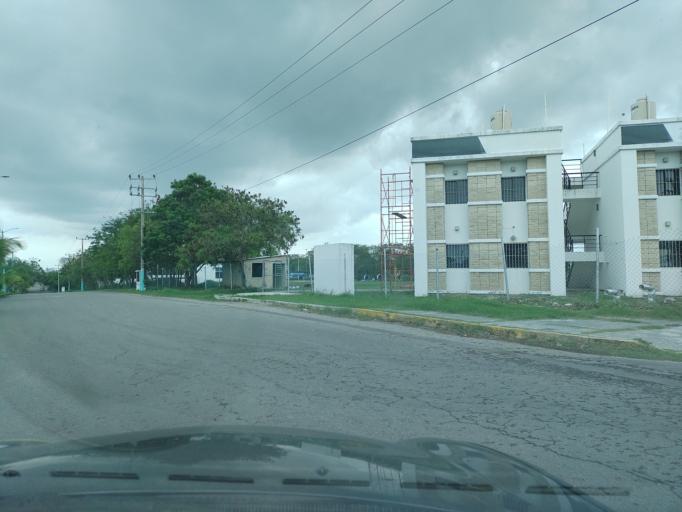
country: MX
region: Quintana Roo
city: Chetumal
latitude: 18.5248
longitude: -88.2730
